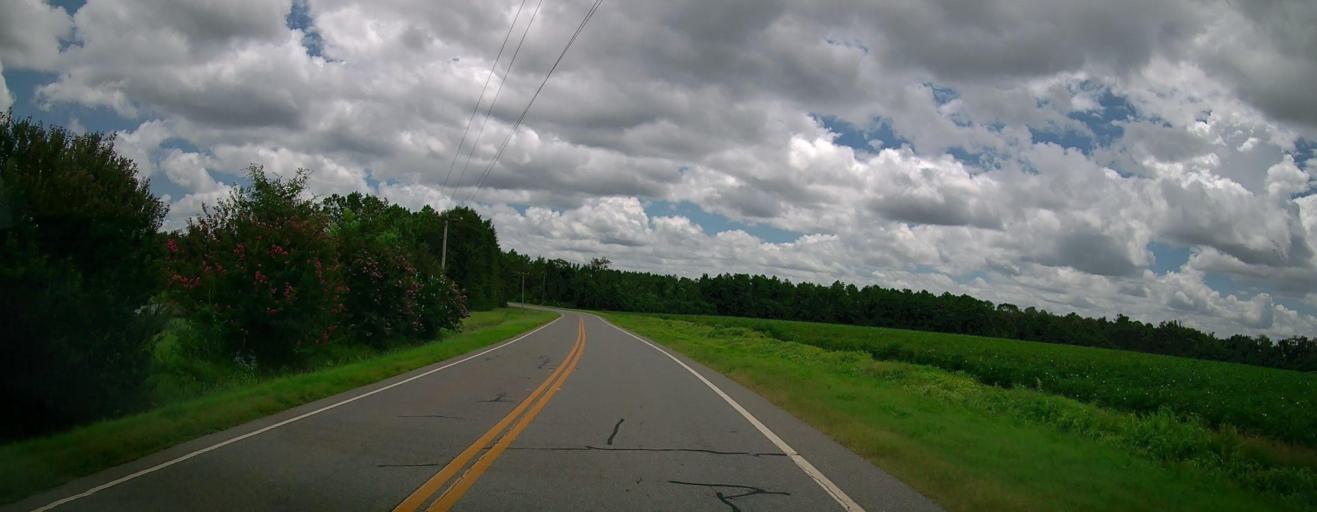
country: US
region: Georgia
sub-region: Wilcox County
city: Rochelle
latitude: 31.9989
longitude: -83.5576
